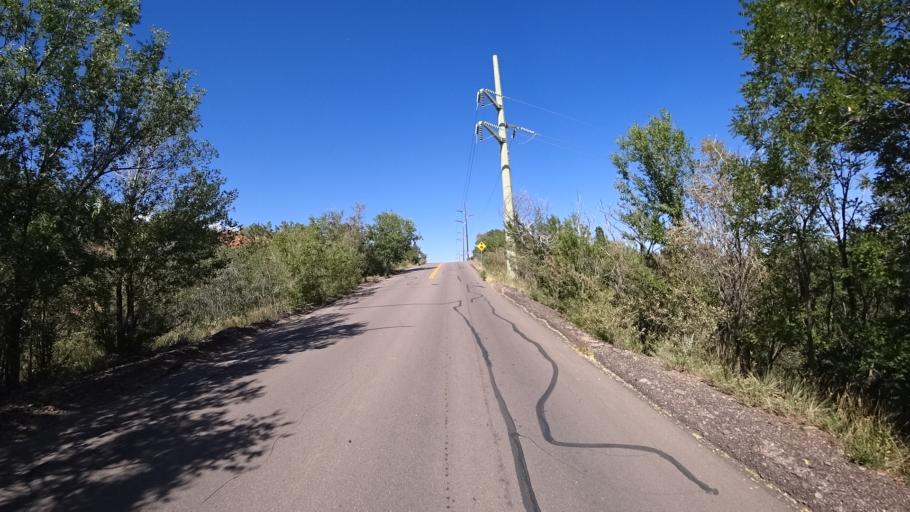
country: US
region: Colorado
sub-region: El Paso County
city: Manitou Springs
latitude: 38.8297
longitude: -104.8798
